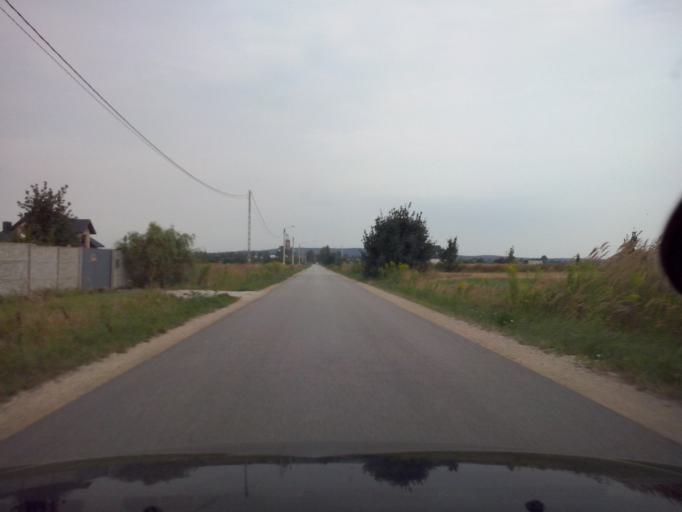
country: PL
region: Swietokrzyskie
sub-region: Powiat kielecki
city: Domaszowice
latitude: 50.8133
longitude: 20.6697
